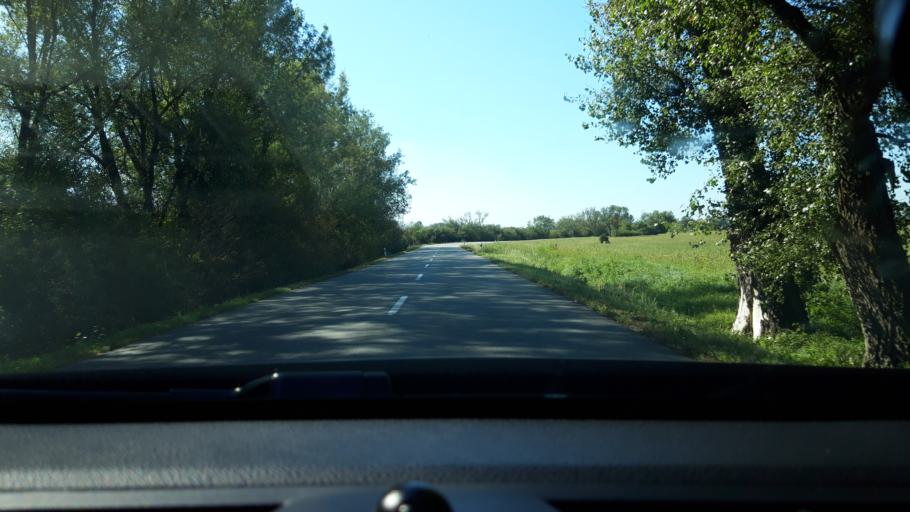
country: SK
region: Kosicky
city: Michalovce
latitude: 48.6502
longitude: 21.9375
